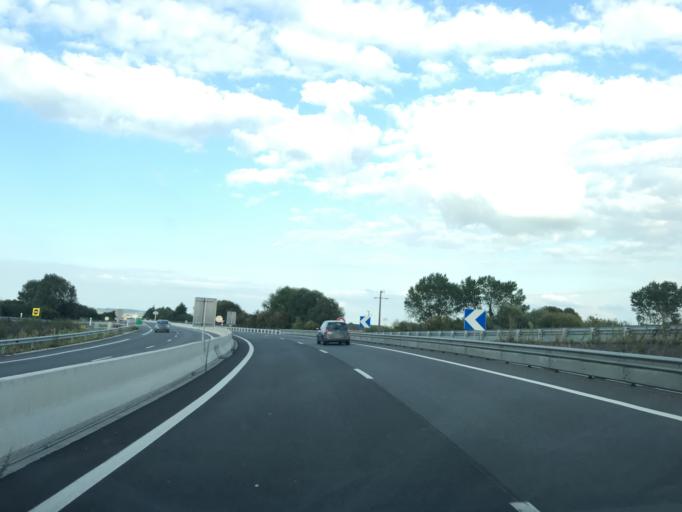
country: FR
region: Haute-Normandie
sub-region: Departement de la Seine-Maritime
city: Tancarville
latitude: 49.4608
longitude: 0.4790
